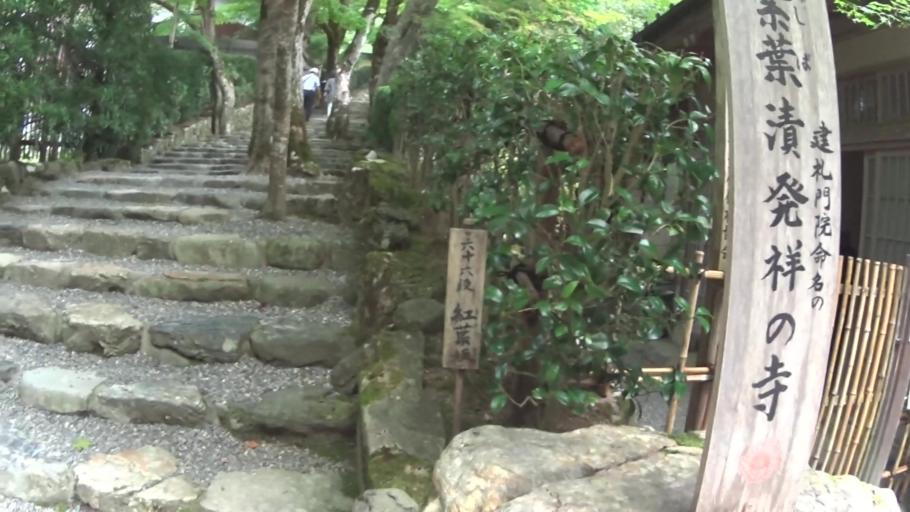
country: JP
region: Shiga Prefecture
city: Kitahama
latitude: 35.1233
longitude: 135.8213
